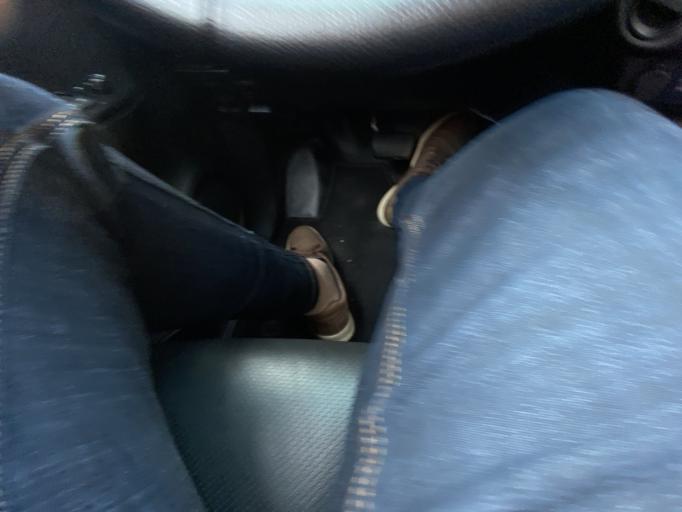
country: ET
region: Adis Abeba
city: Addis Ababa
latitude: 9.0173
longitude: 38.7287
